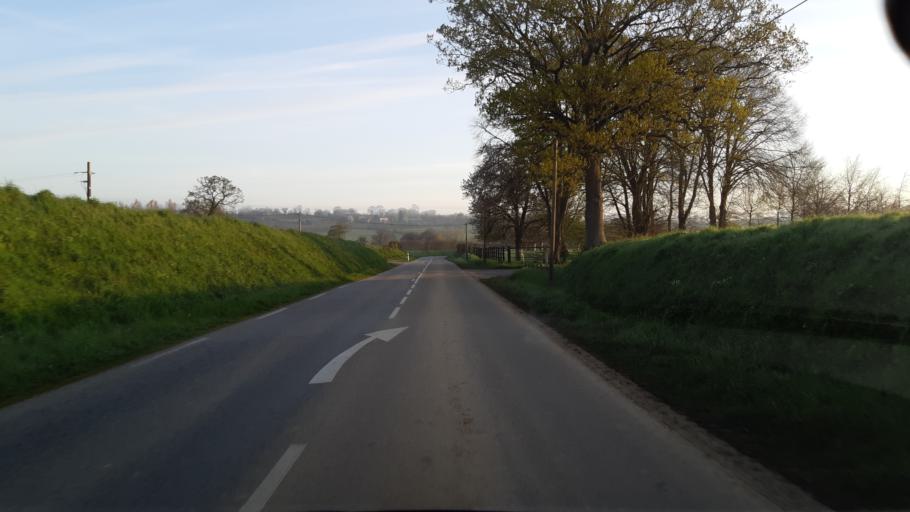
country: FR
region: Lower Normandy
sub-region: Departement de la Manche
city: Agneaux
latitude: 49.0634
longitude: -1.1327
